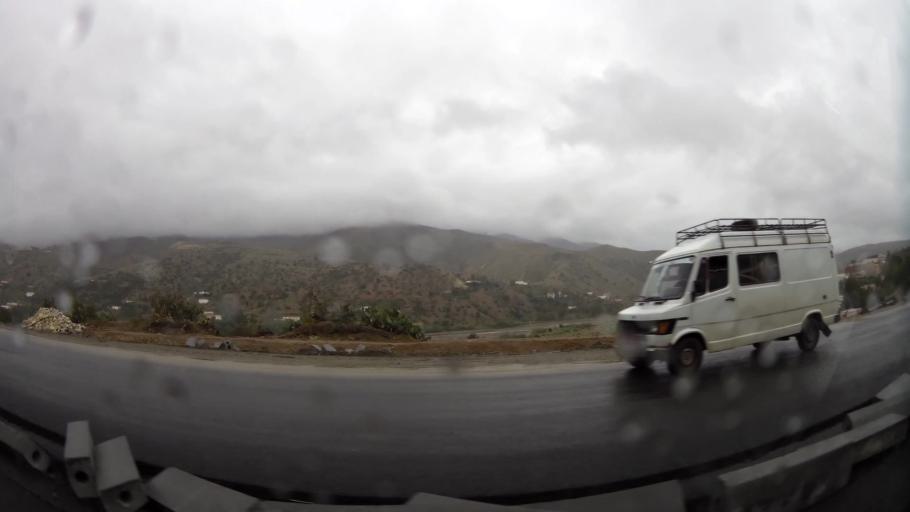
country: MA
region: Taza-Al Hoceima-Taounate
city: Imzourene
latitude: 35.0274
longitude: -3.8218
